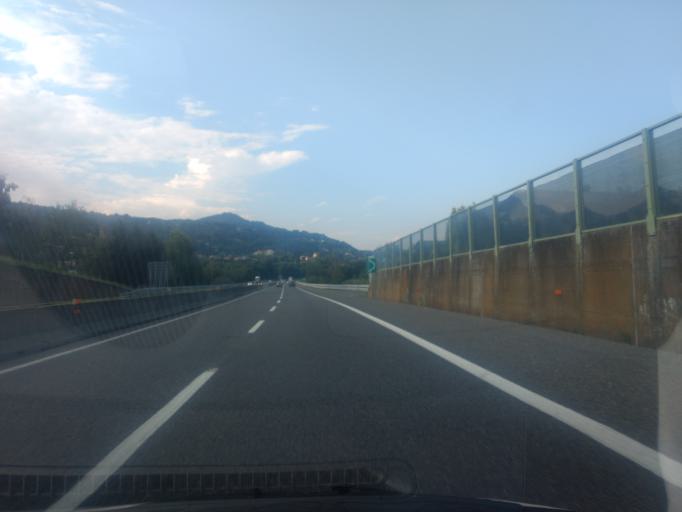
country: IT
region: Piedmont
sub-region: Provincia di Novara
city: Nebbiuno
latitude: 45.7981
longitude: 8.5272
